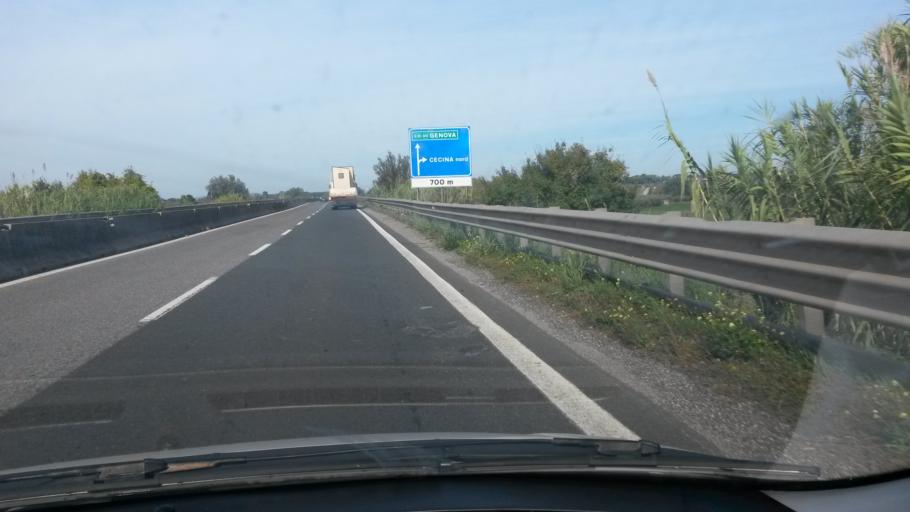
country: IT
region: Tuscany
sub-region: Provincia di Livorno
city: S.P. in Palazzi
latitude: 43.3261
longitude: 10.5293
